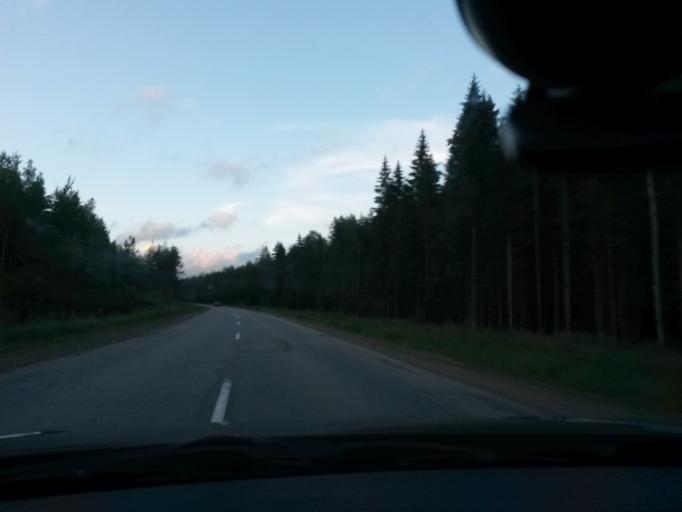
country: LV
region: Jekabpils Rajons
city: Jekabpils
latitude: 56.6751
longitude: 25.9801
